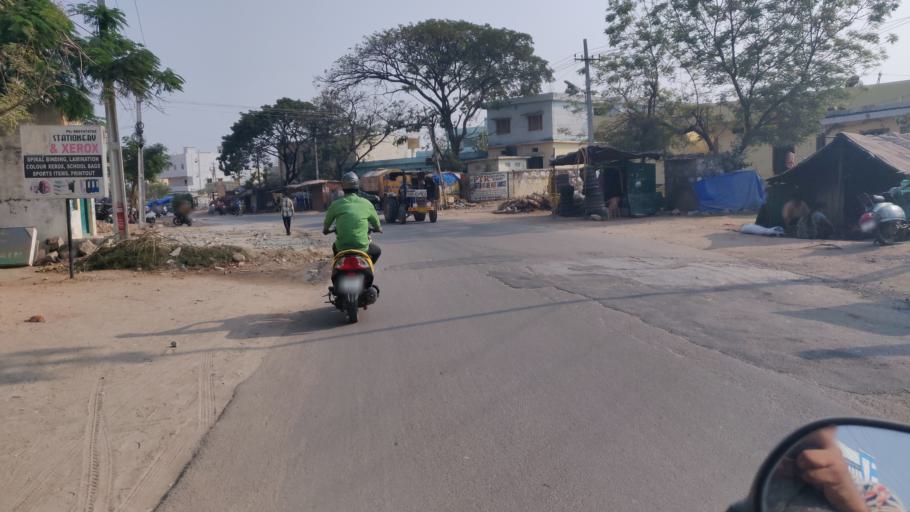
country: IN
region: Telangana
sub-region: Rangareddi
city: Uppal Kalan
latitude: 17.3943
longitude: 78.5944
